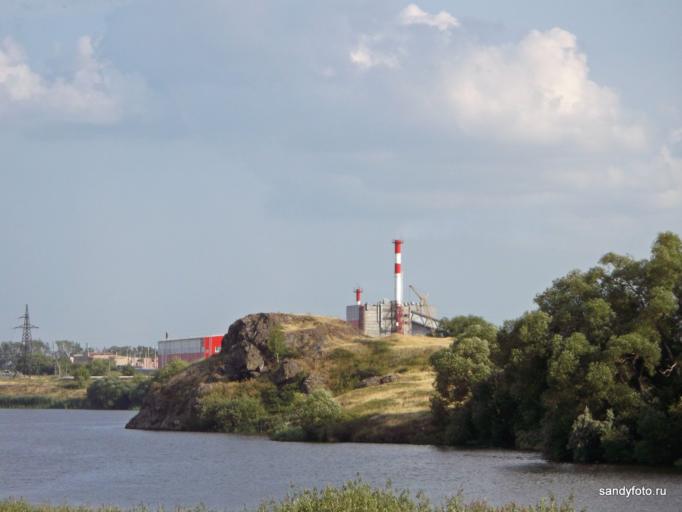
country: RU
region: Chelyabinsk
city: Troitsk
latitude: 54.0758
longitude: 61.5761
